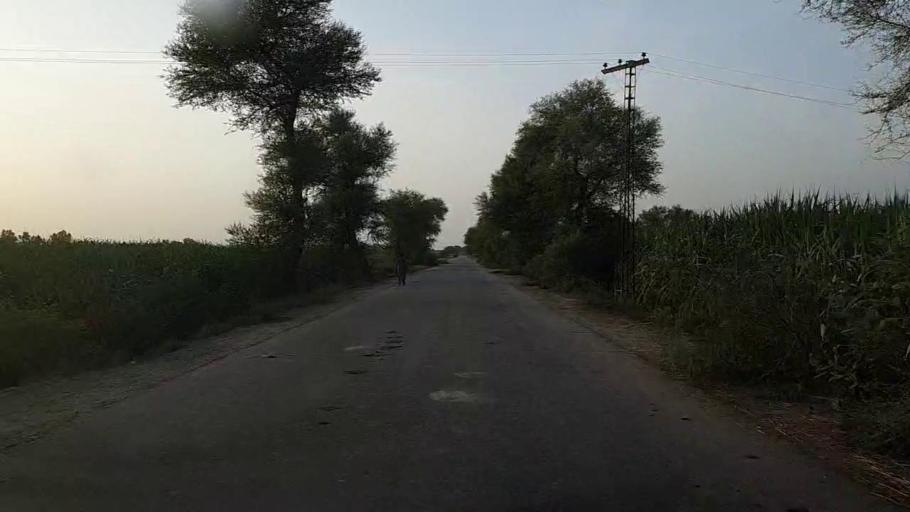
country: PK
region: Sindh
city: Ubauro
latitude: 28.2245
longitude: 69.8188
